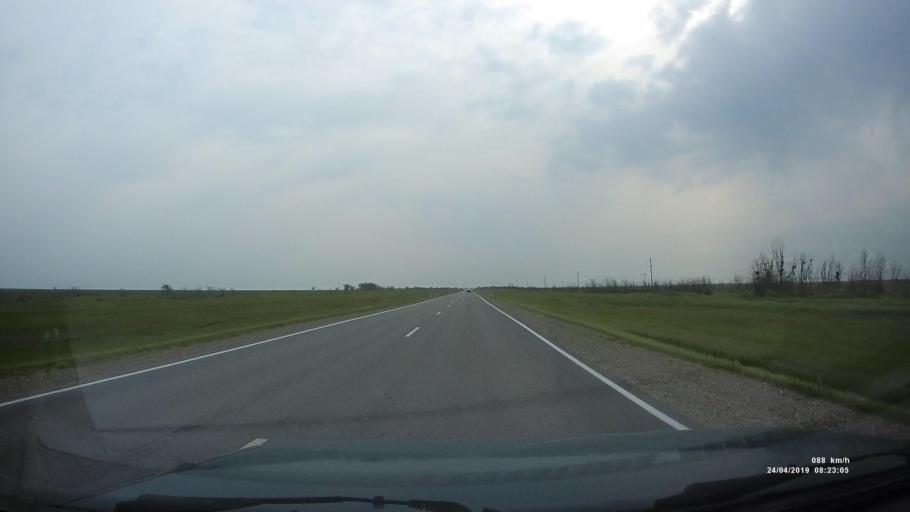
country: RU
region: Kalmykiya
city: Priyutnoye
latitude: 46.1161
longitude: 43.7302
